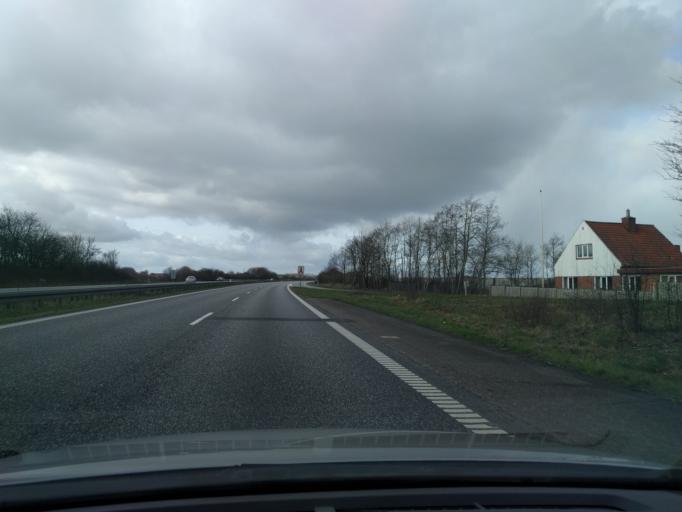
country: DK
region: South Denmark
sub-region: Fredericia Kommune
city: Taulov
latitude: 55.5399
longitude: 9.6372
